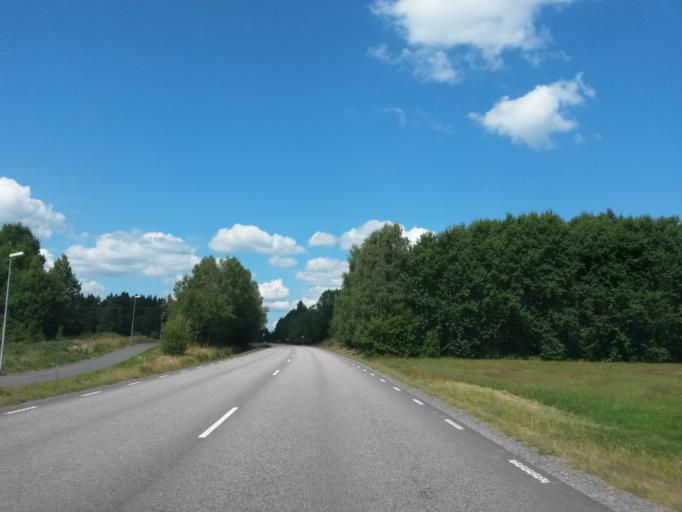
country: SE
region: Vaestra Goetaland
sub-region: Lerums Kommun
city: Grabo
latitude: 57.8199
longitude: 12.2994
